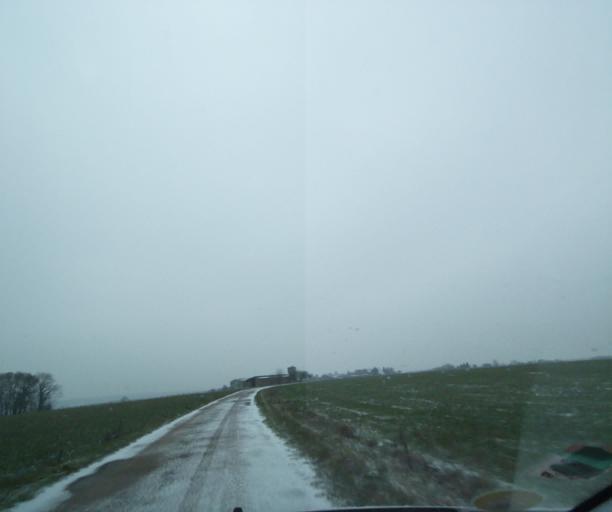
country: FR
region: Champagne-Ardenne
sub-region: Departement de la Haute-Marne
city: Wassy
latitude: 48.4665
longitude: 5.0018
